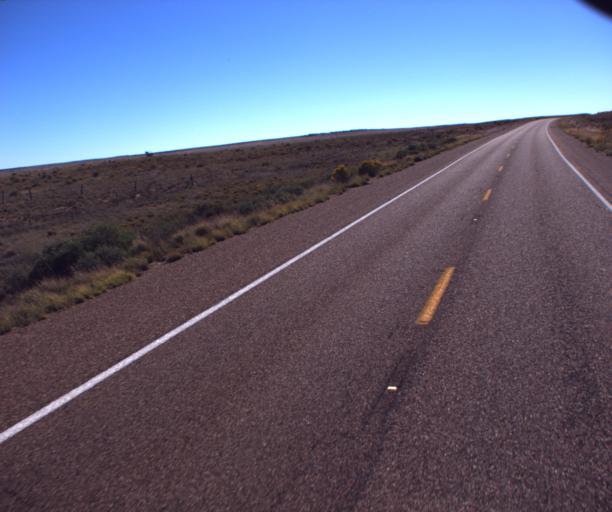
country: US
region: Arizona
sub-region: Navajo County
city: Holbrook
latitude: 34.8417
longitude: -109.9474
